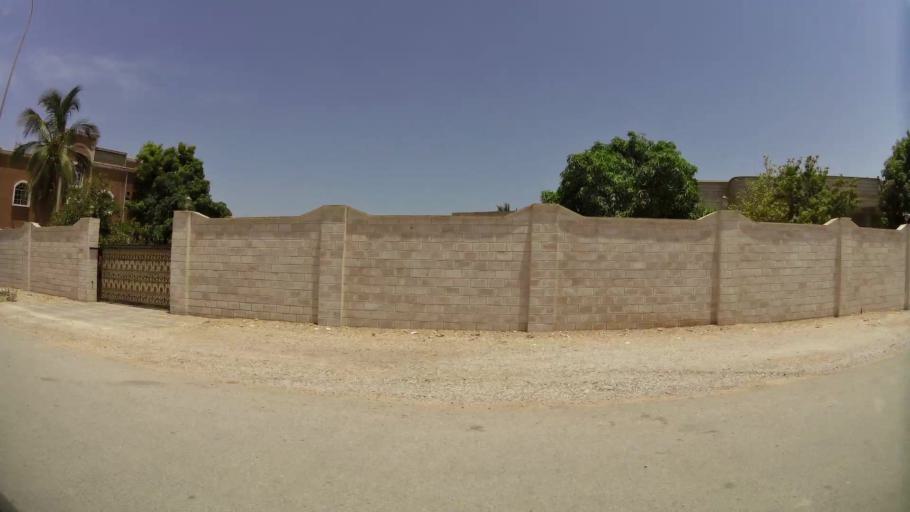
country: OM
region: Zufar
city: Salalah
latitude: 17.0785
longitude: 54.1517
